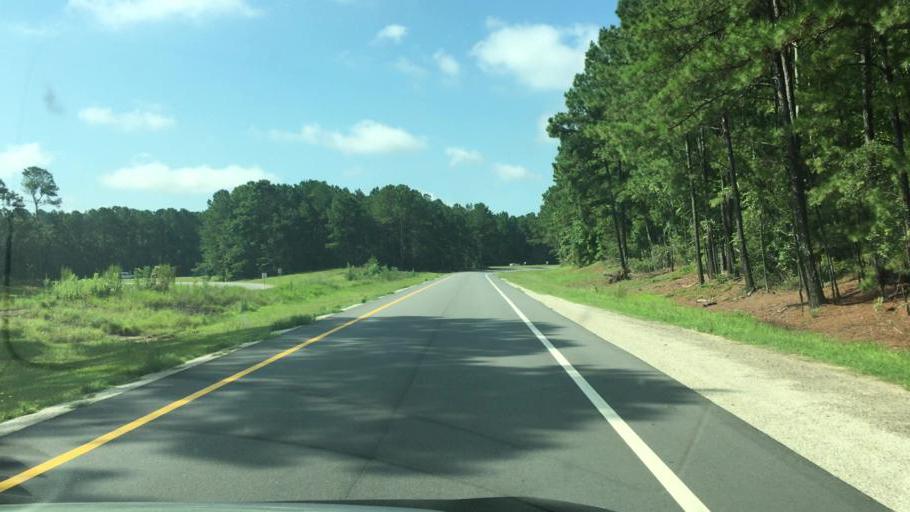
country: US
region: North Carolina
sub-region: Cumberland County
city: Fayetteville
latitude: 34.9783
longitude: -78.8593
